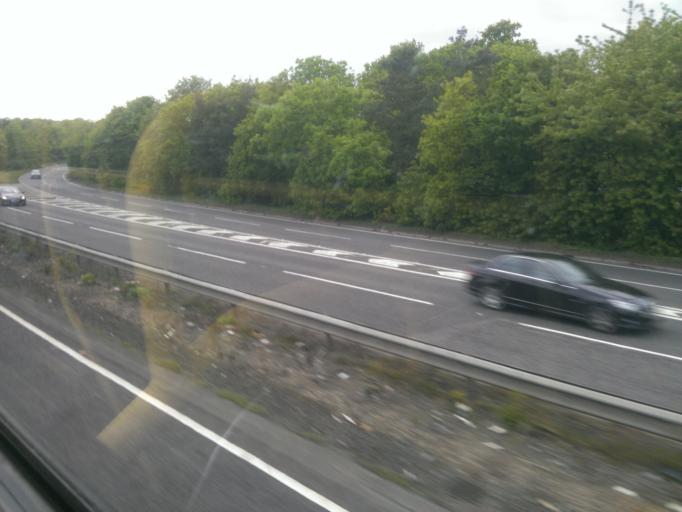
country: GB
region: England
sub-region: Essex
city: Colchester
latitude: 51.9274
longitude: 0.9417
